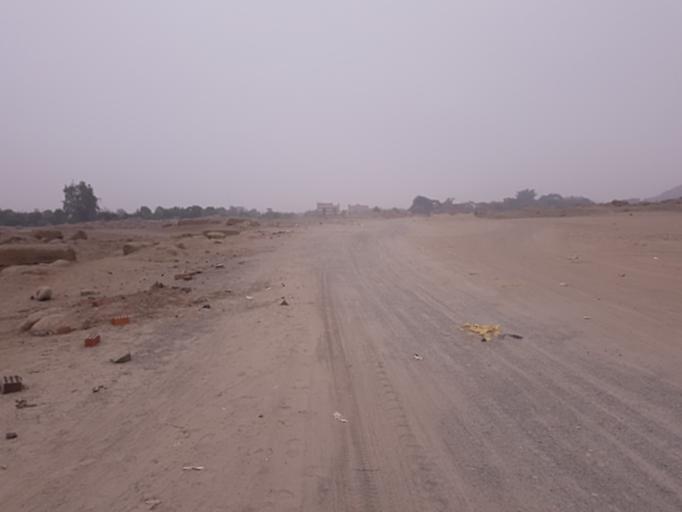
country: PE
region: Lima
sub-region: Lima
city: Santa Maria
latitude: -11.9853
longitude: -76.9115
